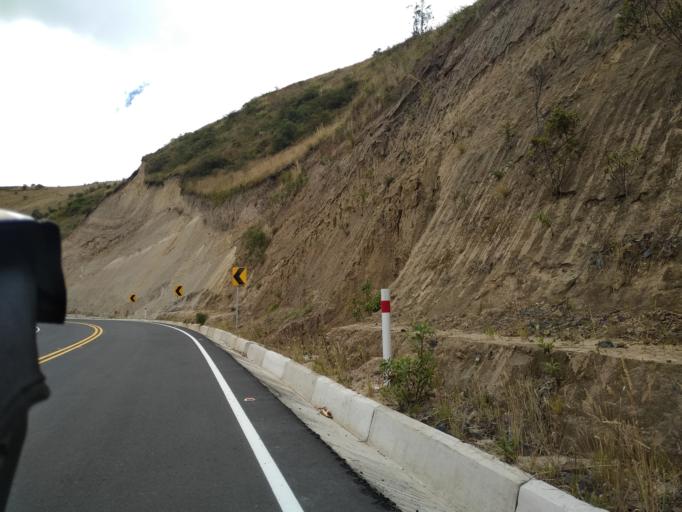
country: EC
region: Cotopaxi
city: Saquisili
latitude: -0.7801
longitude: -78.9107
